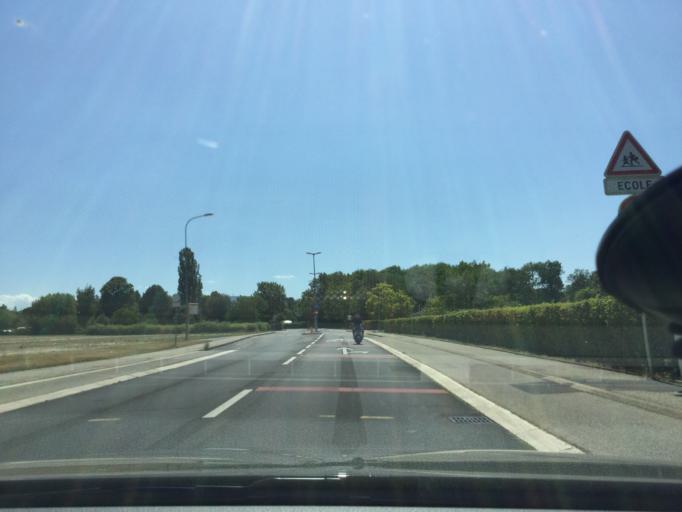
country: CH
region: Geneva
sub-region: Geneva
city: Vandoeuvres
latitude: 46.2491
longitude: 6.2010
